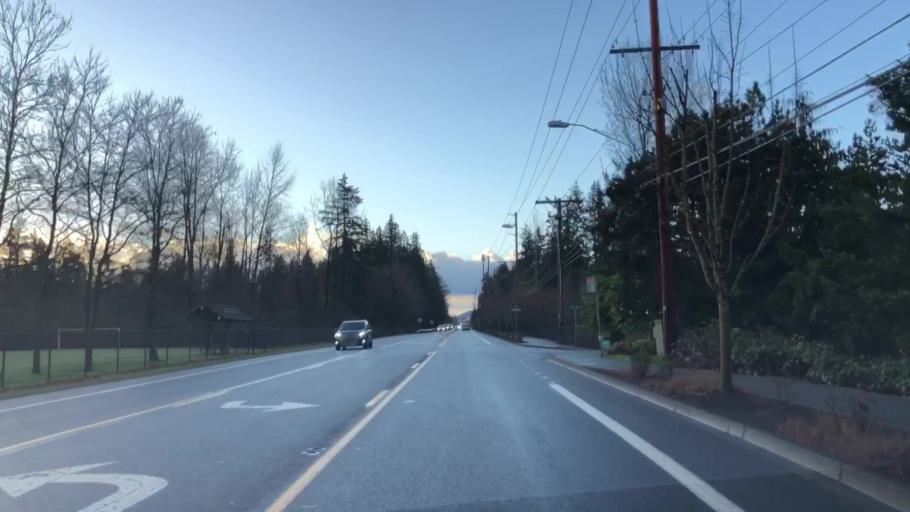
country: US
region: Washington
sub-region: King County
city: City of Sammamish
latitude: 47.6260
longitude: -122.0355
